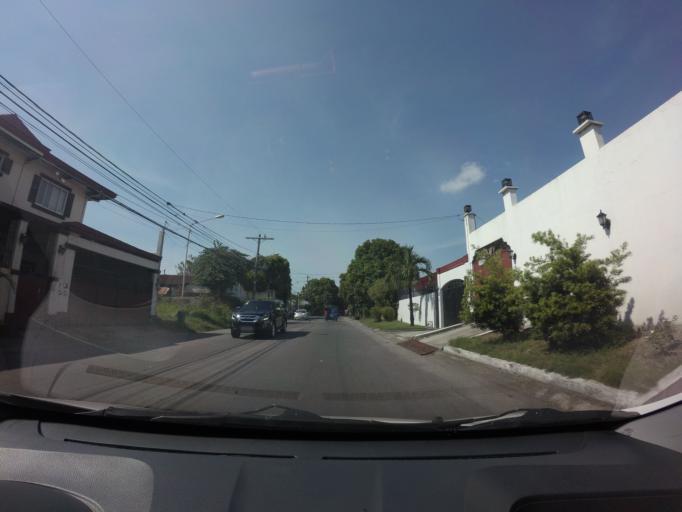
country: PH
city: Sambayanihan People's Village
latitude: 14.4454
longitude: 121.0076
